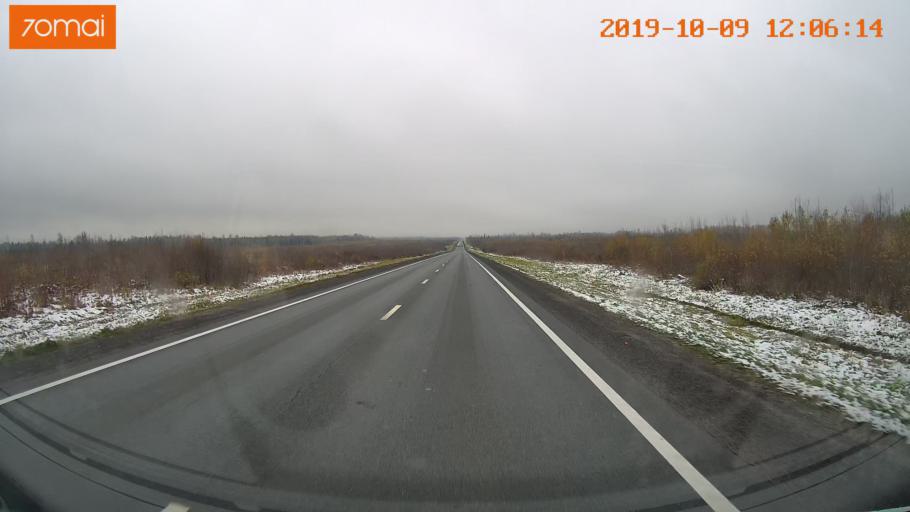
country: RU
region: Jaroslavl
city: Prechistoye
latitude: 58.6174
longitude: 40.3338
